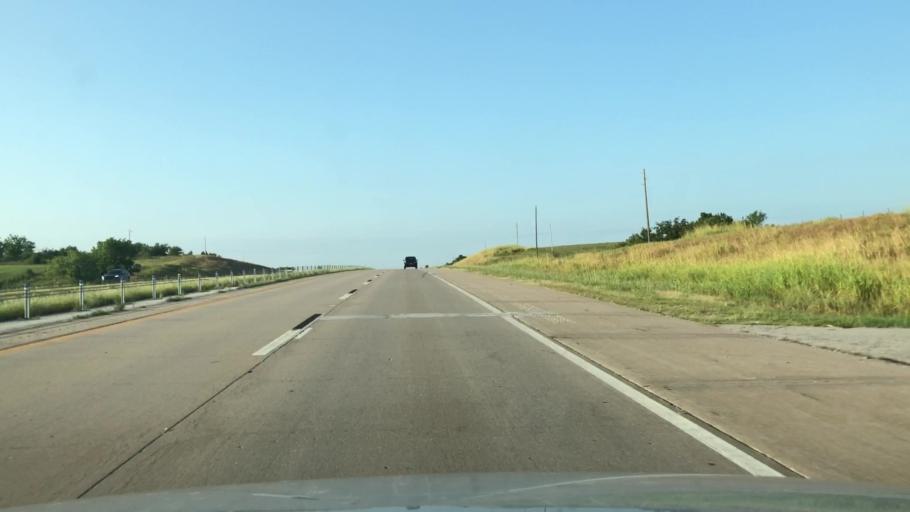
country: US
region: Oklahoma
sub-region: Osage County
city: Skiatook
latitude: 36.4807
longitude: -95.9207
